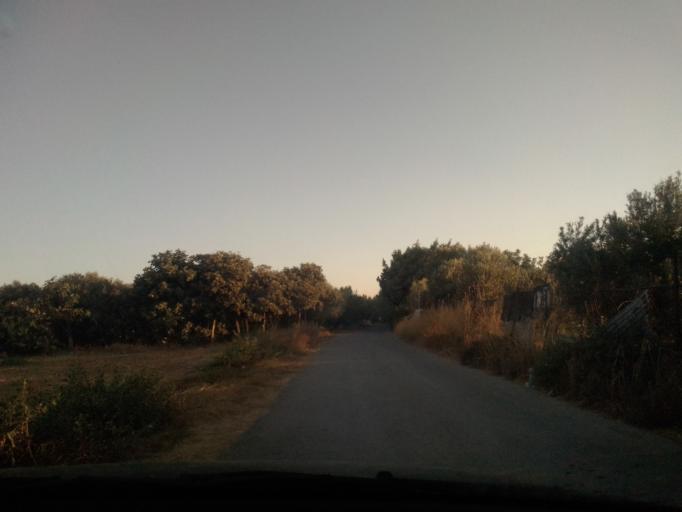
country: CY
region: Limassol
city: Ypsonas
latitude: 34.6731
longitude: 32.9684
